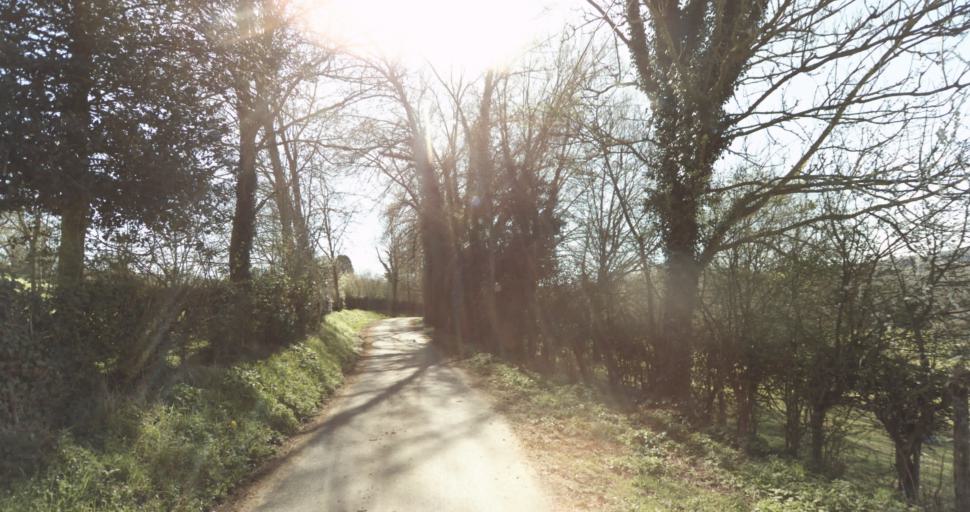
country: FR
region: Lower Normandy
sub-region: Departement du Calvados
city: Livarot
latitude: 48.9932
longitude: 0.0751
